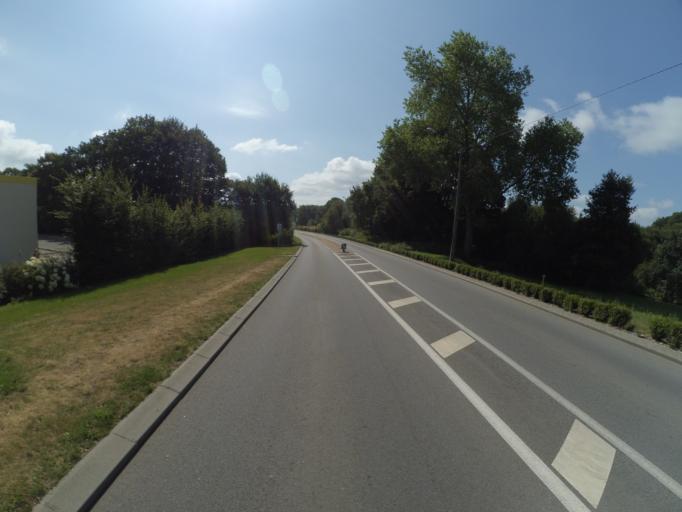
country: FR
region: Brittany
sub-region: Departement du Finistere
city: Bannalec
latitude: 47.9268
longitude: -3.6869
